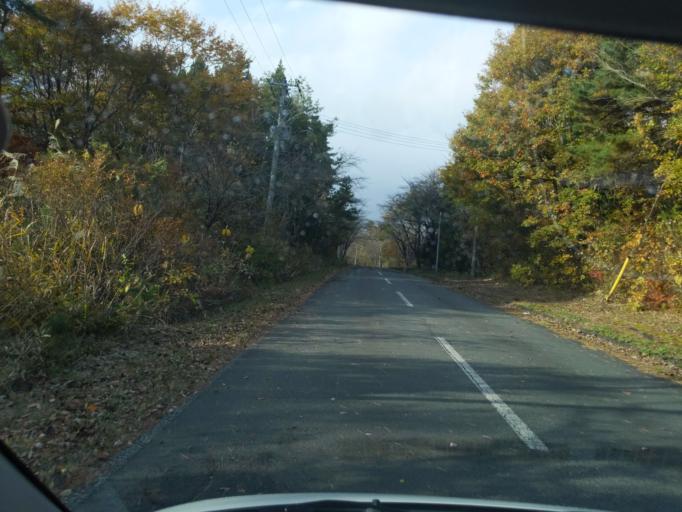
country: JP
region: Iwate
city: Mizusawa
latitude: 39.0314
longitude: 141.0874
